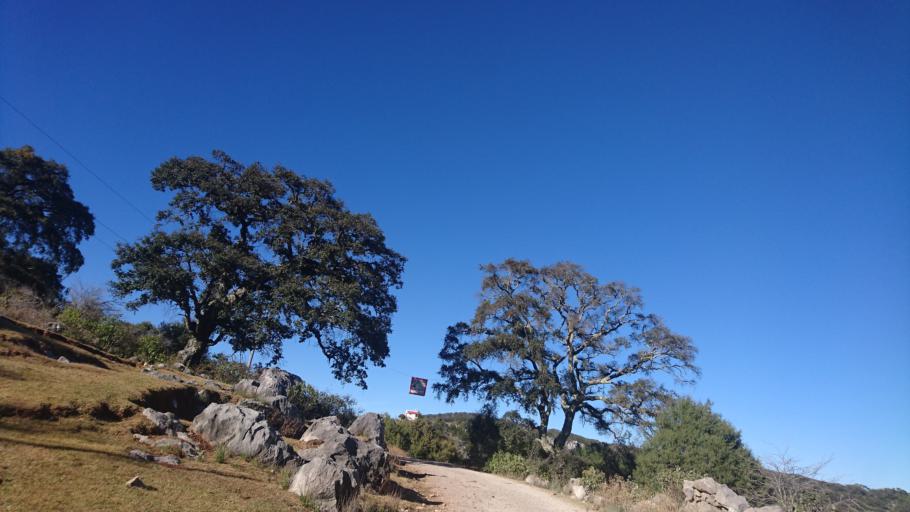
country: MX
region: San Luis Potosi
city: Zaragoza
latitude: 22.0250
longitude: -100.6027
